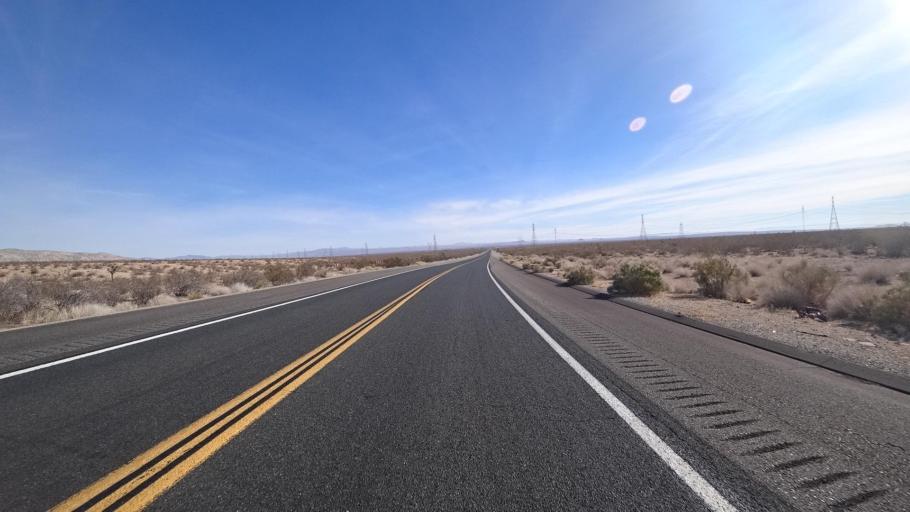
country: US
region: California
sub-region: Kern County
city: Mojave
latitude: 35.1248
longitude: -118.1691
